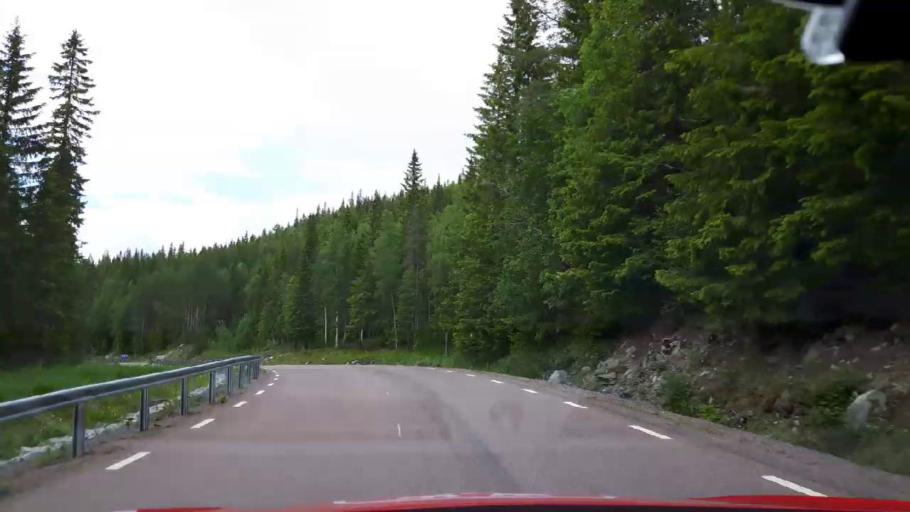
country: SE
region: Jaemtland
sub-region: Krokoms Kommun
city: Valla
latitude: 64.0850
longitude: 14.0706
